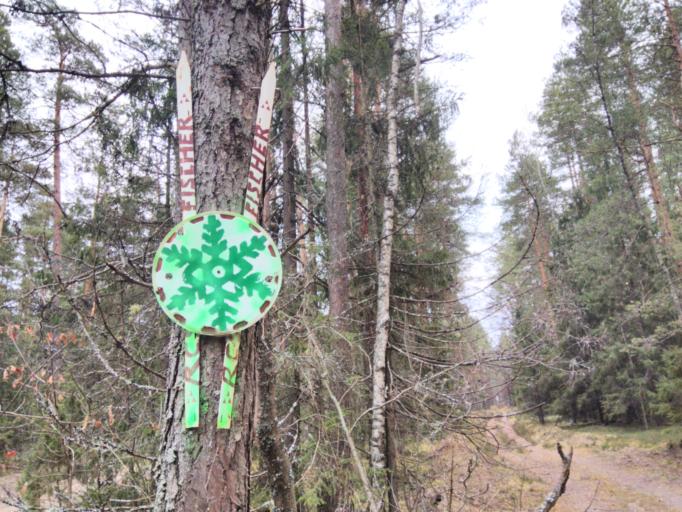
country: RU
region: Vladimir
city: Sobinka
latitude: 55.9797
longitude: 40.0744
